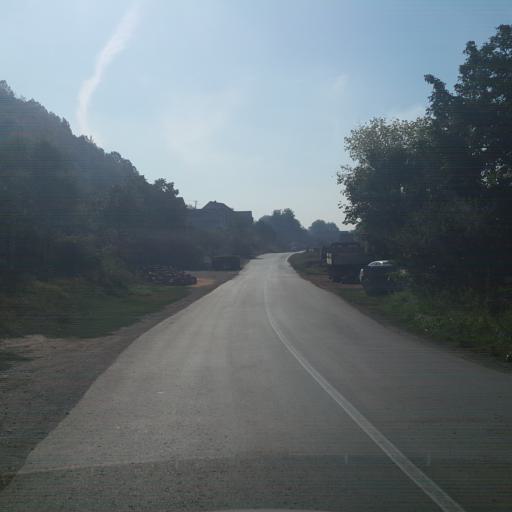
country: RS
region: Central Serbia
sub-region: Pirotski Okrug
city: Pirot
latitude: 43.1877
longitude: 22.5707
